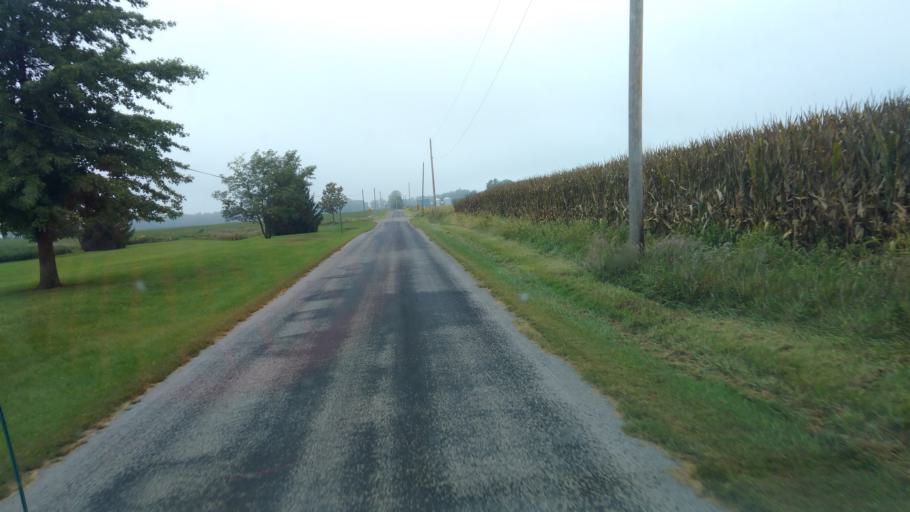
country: US
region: Ohio
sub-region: Hardin County
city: Kenton
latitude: 40.5208
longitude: -83.6008
